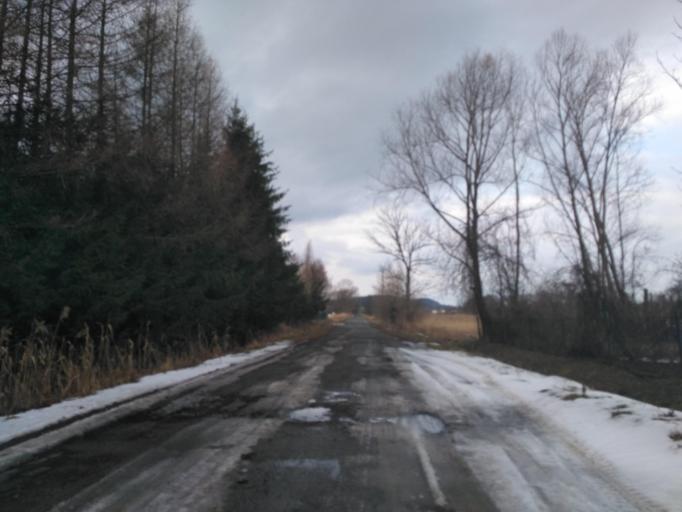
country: PL
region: Subcarpathian Voivodeship
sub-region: Powiat sanocki
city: Strachocina
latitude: 49.6026
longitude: 22.1358
